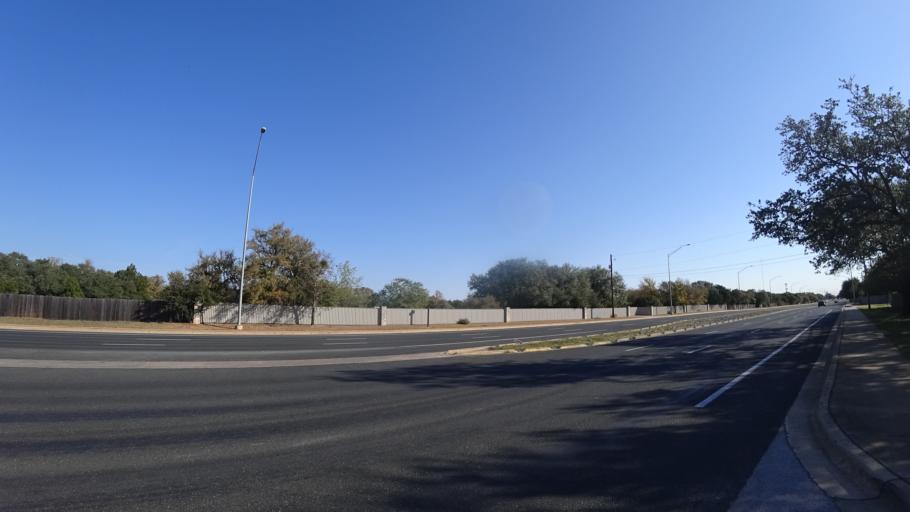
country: US
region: Texas
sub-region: Travis County
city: Shady Hollow
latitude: 30.2248
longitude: -97.8493
